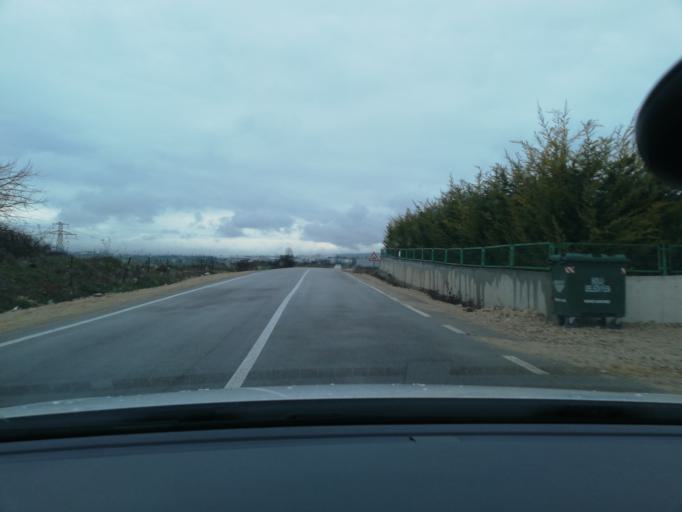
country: TR
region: Bolu
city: Bolu
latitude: 40.7645
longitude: 31.6599
